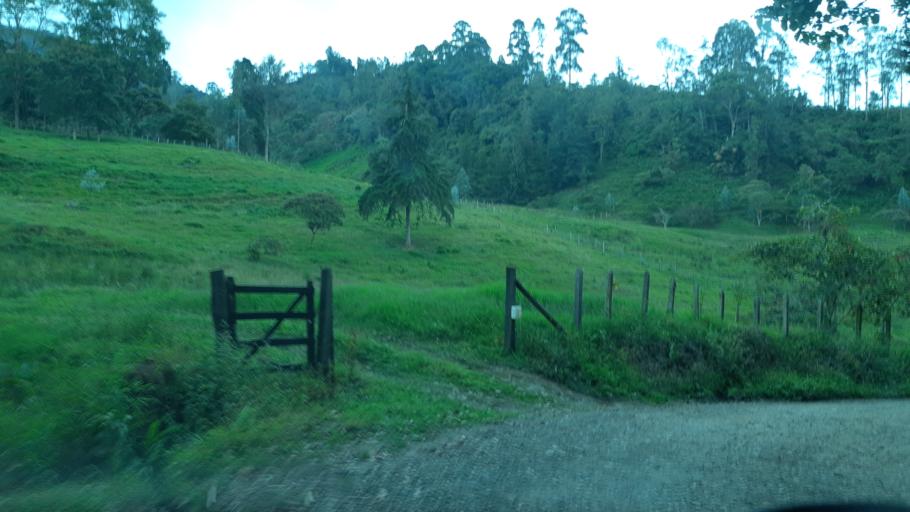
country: CO
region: Boyaca
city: Garagoa
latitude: 5.1128
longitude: -73.3505
